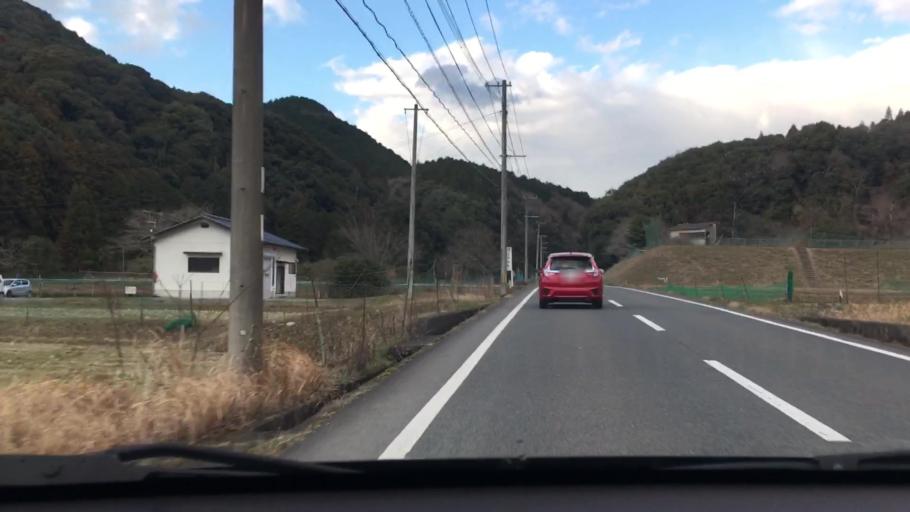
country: JP
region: Oita
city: Bungo-Takada-shi
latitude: 33.4505
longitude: 131.3932
